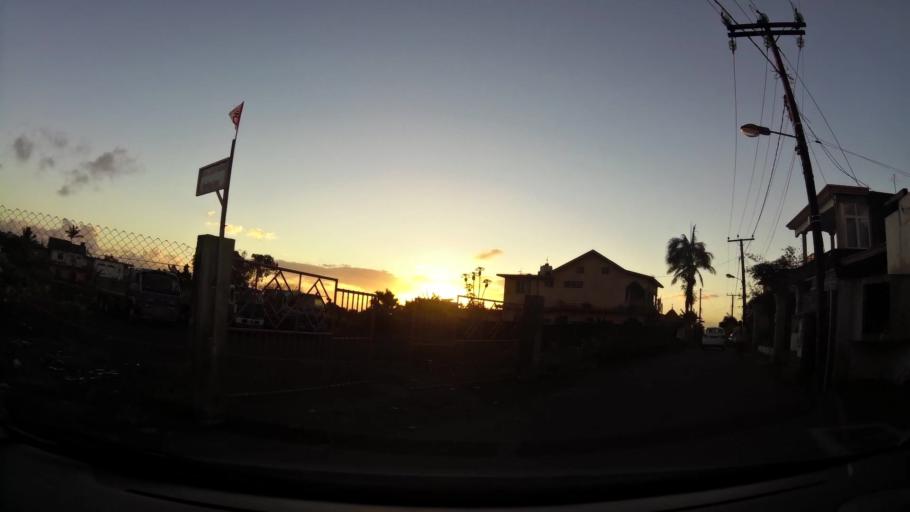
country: MU
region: Plaines Wilhems
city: Curepipe
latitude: -20.3019
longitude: 57.5238
